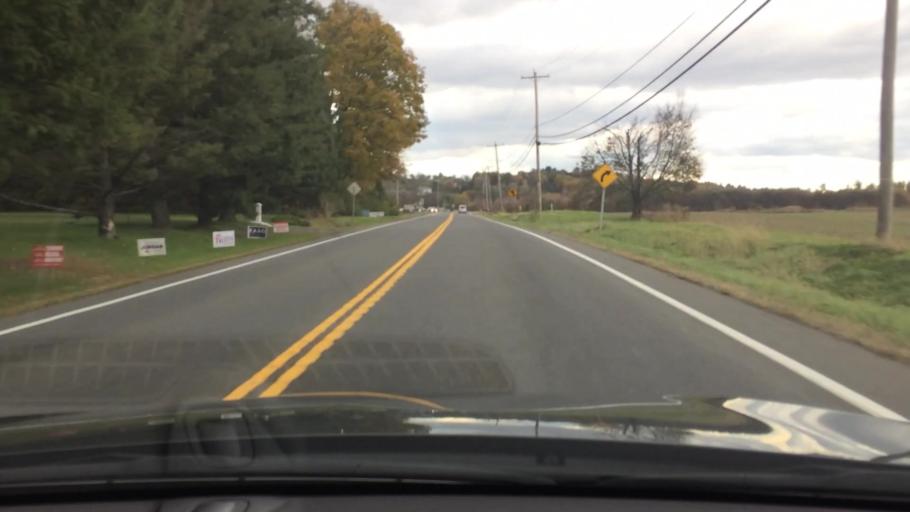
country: US
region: New York
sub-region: Columbia County
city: Oakdale
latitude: 42.2101
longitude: -73.7310
